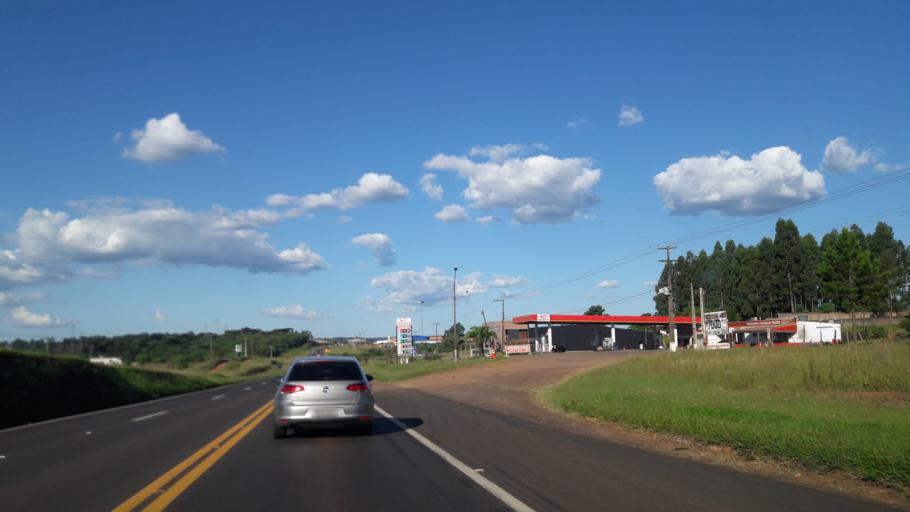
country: BR
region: Parana
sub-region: Guarapuava
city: Guarapuava
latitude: -25.3771
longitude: -51.5051
